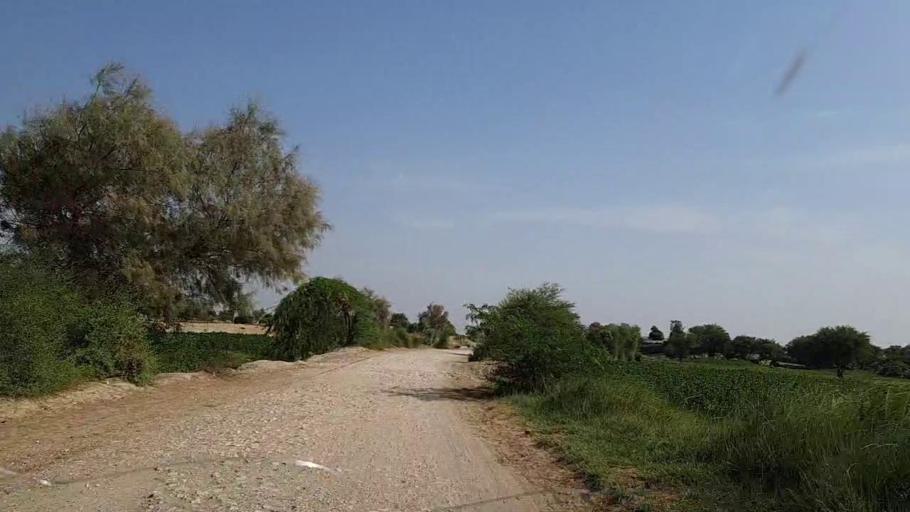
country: PK
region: Sindh
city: Khanpur
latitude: 27.7313
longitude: 69.3583
